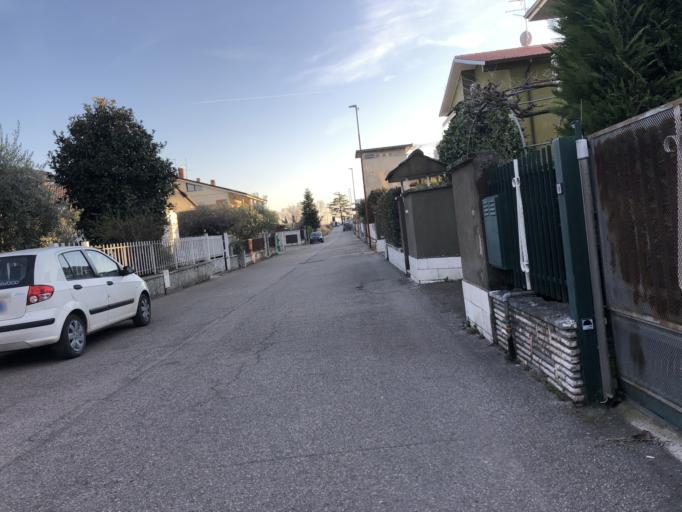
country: IT
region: Veneto
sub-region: Provincia di Verona
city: Pastrengo
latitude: 45.4763
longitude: 10.8230
